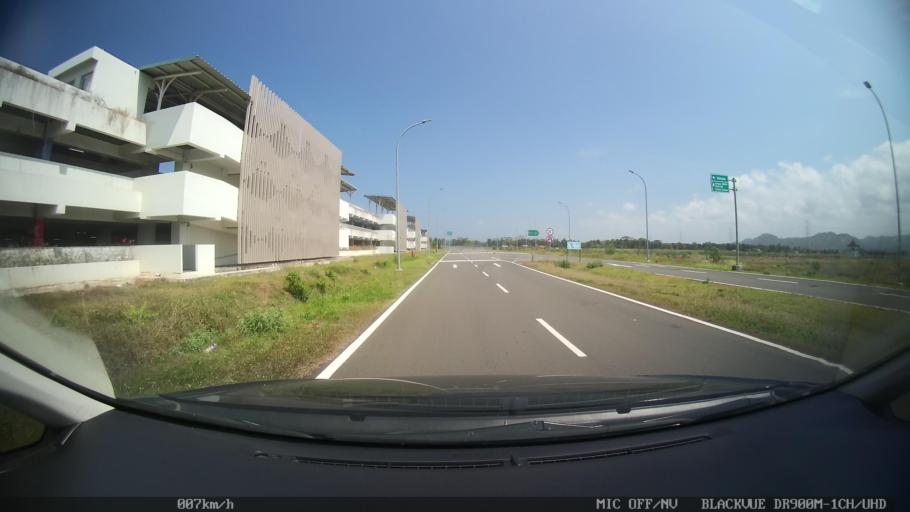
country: ID
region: Daerah Istimewa Yogyakarta
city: Srandakan
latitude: -7.8958
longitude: 110.0613
